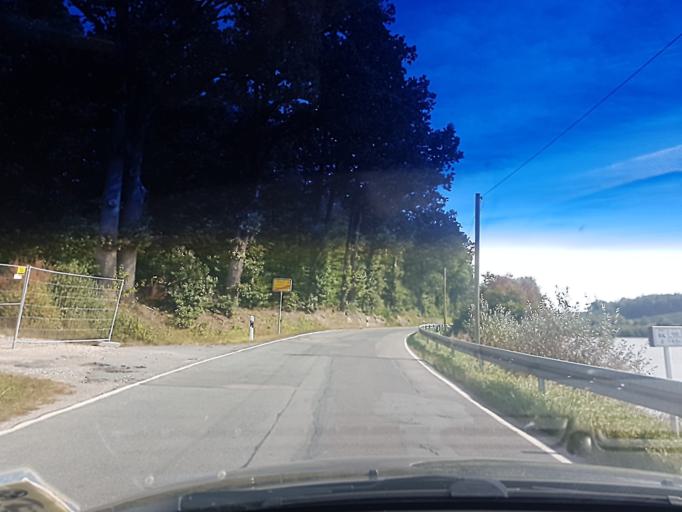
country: DE
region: Bavaria
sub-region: Regierungsbezirk Mittelfranken
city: Wachenroth
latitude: 49.7821
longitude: 10.7023
